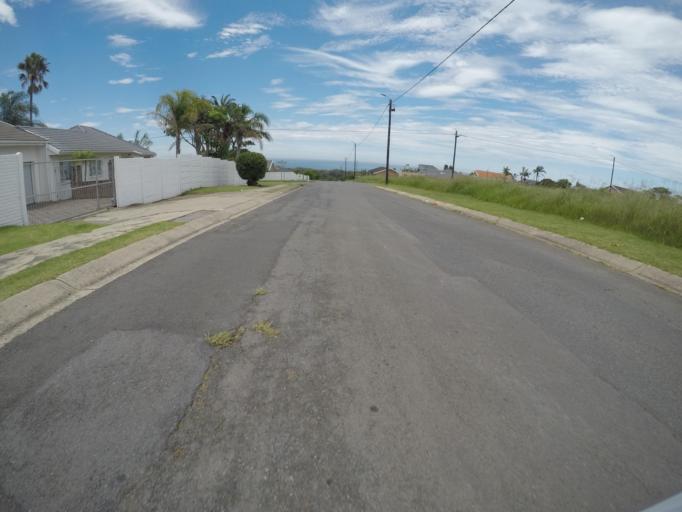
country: ZA
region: Eastern Cape
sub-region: Buffalo City Metropolitan Municipality
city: East London
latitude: -33.0393
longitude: 27.8570
